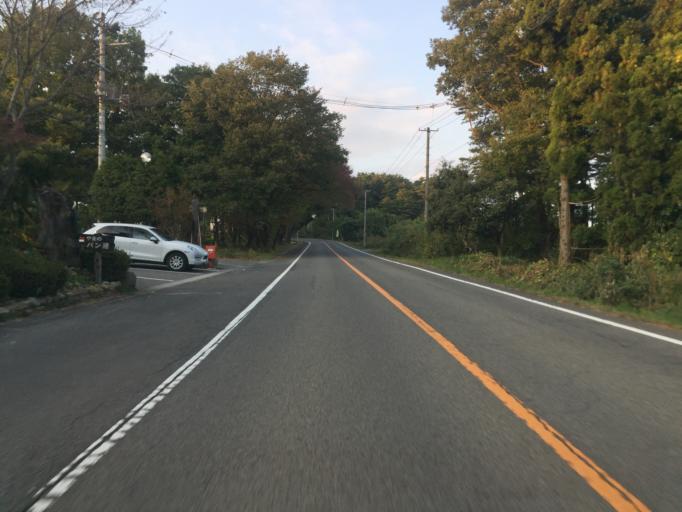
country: JP
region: Fukushima
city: Motomiya
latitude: 37.5749
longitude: 140.3520
